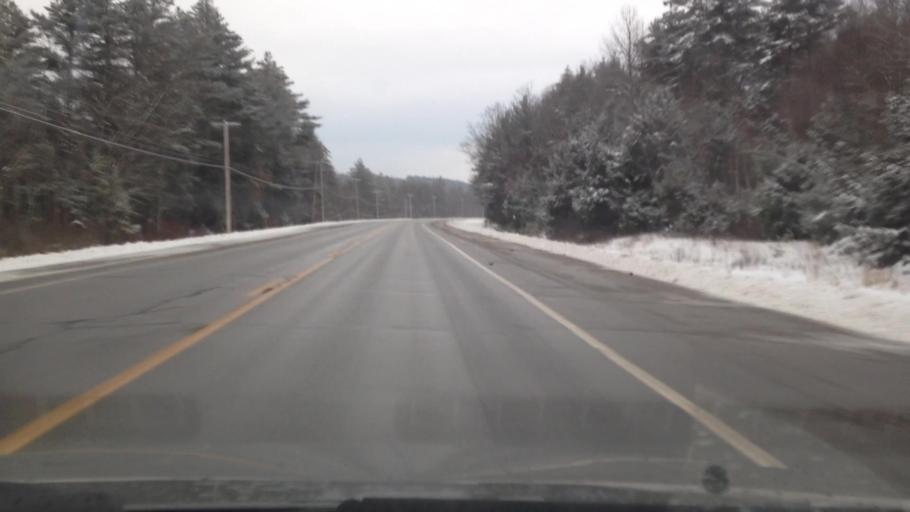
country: US
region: New Hampshire
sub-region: Cheshire County
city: Keene
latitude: 42.9833
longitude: -72.2573
